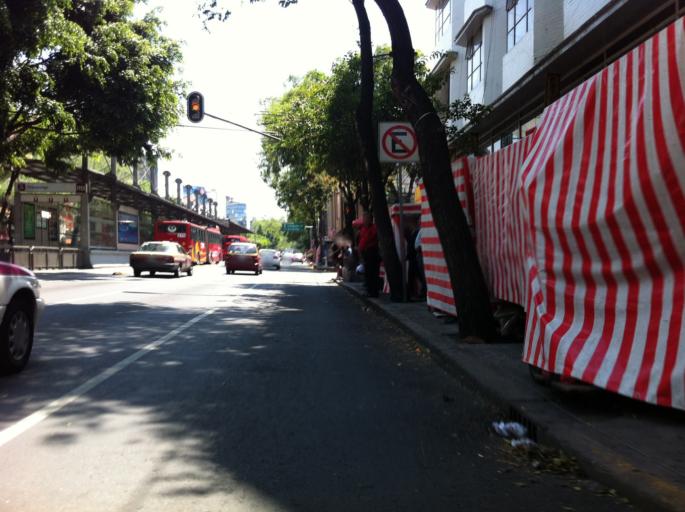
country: MX
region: Mexico City
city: Benito Juarez
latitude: 19.4076
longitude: -99.1678
